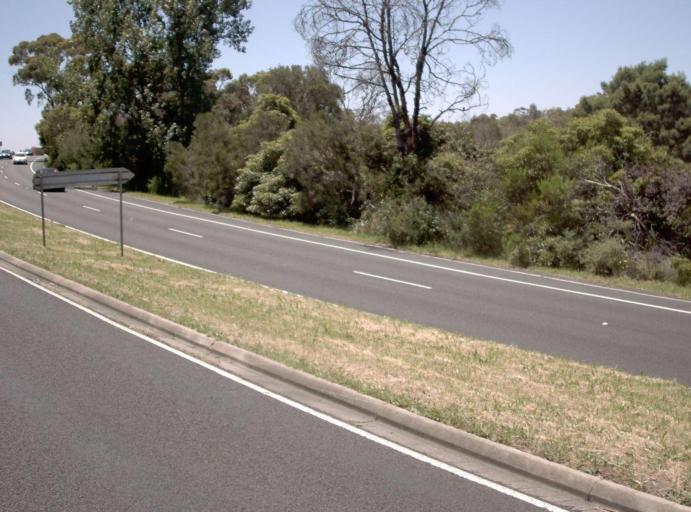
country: AU
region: Victoria
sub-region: Mornington Peninsula
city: Mount Eliza
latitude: -38.1808
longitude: 145.0957
